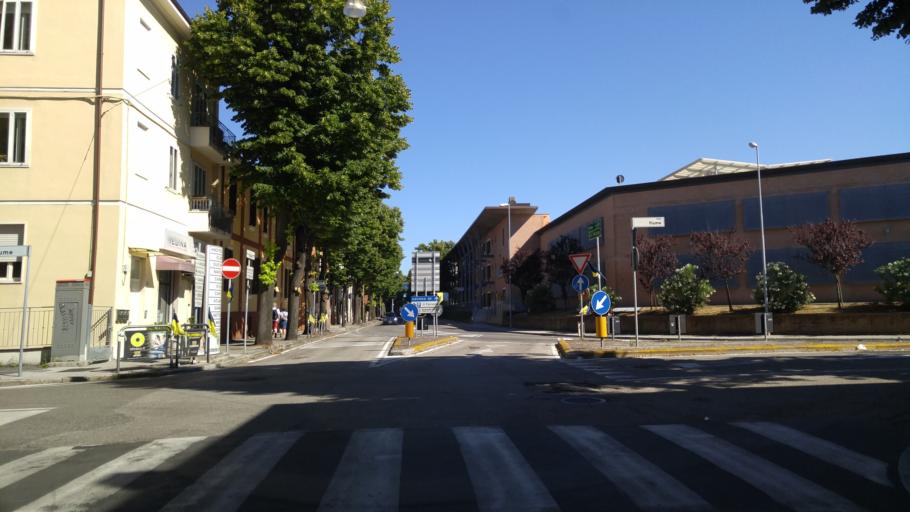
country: IT
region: The Marches
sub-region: Provincia di Pesaro e Urbino
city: Pesaro
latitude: 43.9157
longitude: 12.9106
